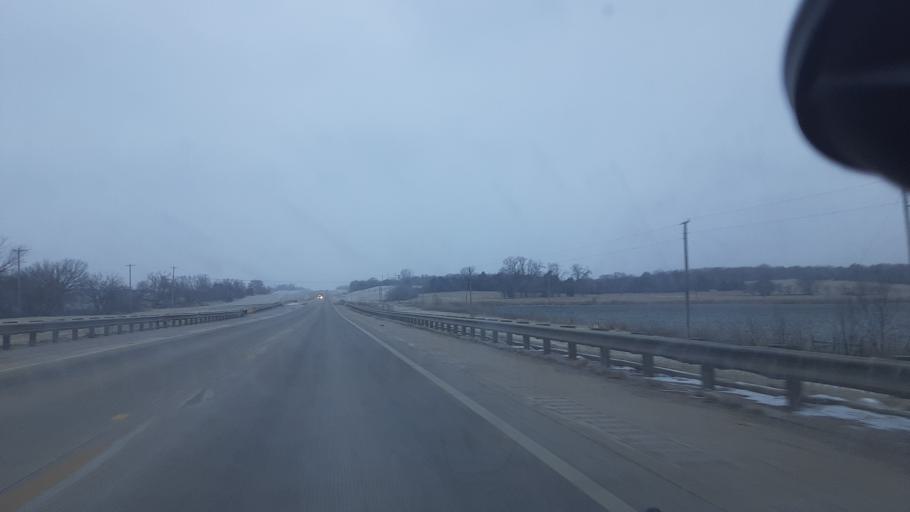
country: US
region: Oklahoma
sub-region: Payne County
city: Perkins
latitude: 35.9859
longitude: -97.1197
